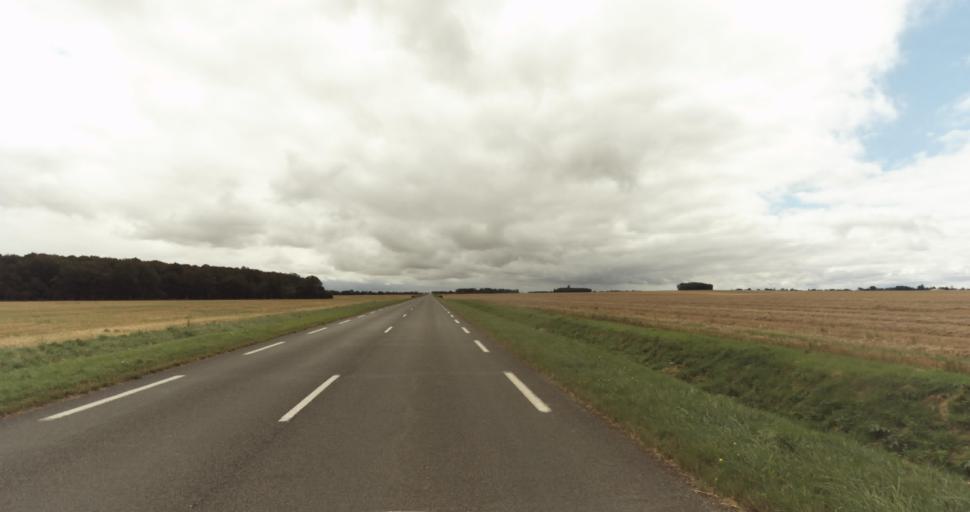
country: FR
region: Haute-Normandie
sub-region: Departement de l'Eure
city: Arnieres-sur-Iton
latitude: 48.9412
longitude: 1.1641
